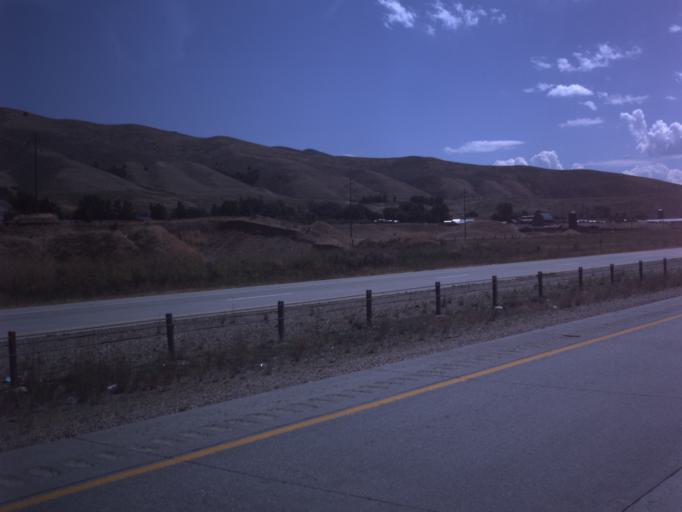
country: US
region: Utah
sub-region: Morgan County
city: Mountain Green
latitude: 41.1045
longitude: -111.7464
